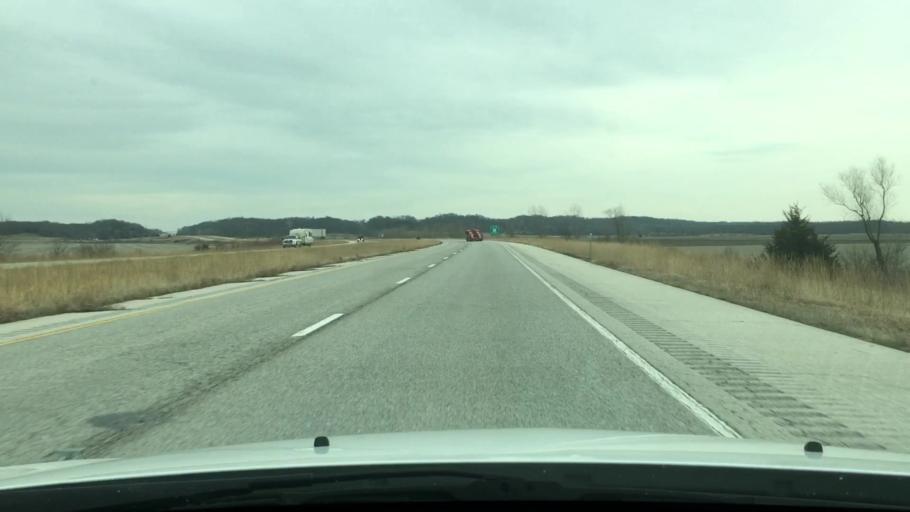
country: US
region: Illinois
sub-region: Pike County
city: Griggsville
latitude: 39.6867
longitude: -90.5927
